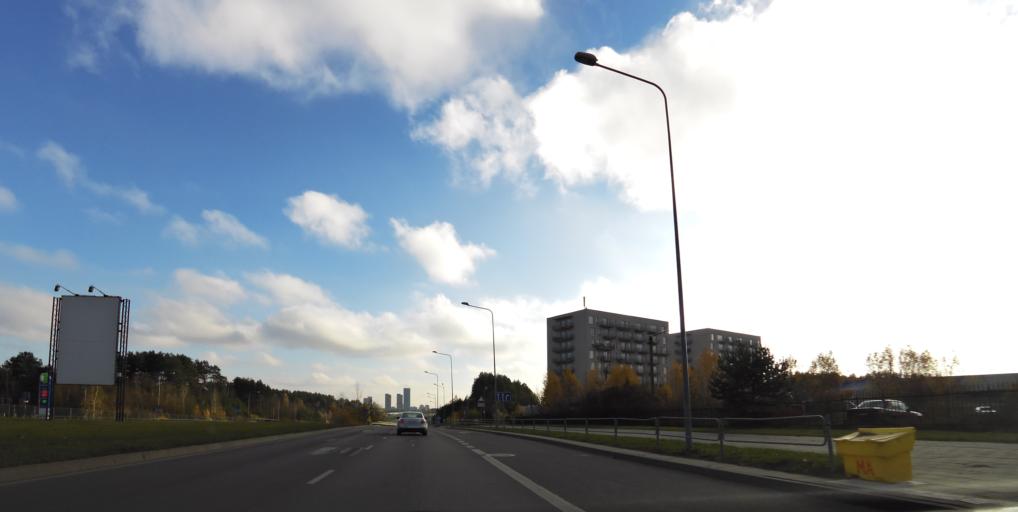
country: LT
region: Vilnius County
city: Pilaite
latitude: 54.7086
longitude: 25.1879
